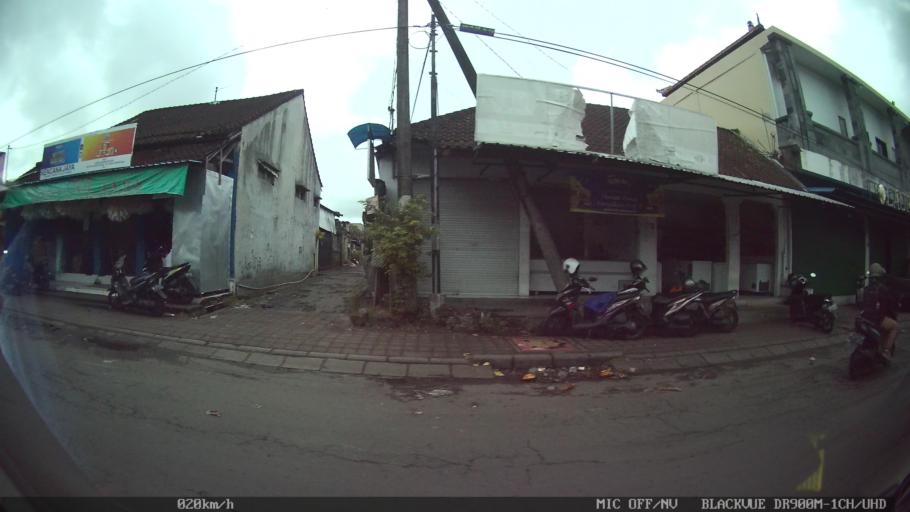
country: ID
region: Bali
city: Banjar Mambalkajanan
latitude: -8.5503
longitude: 115.2199
